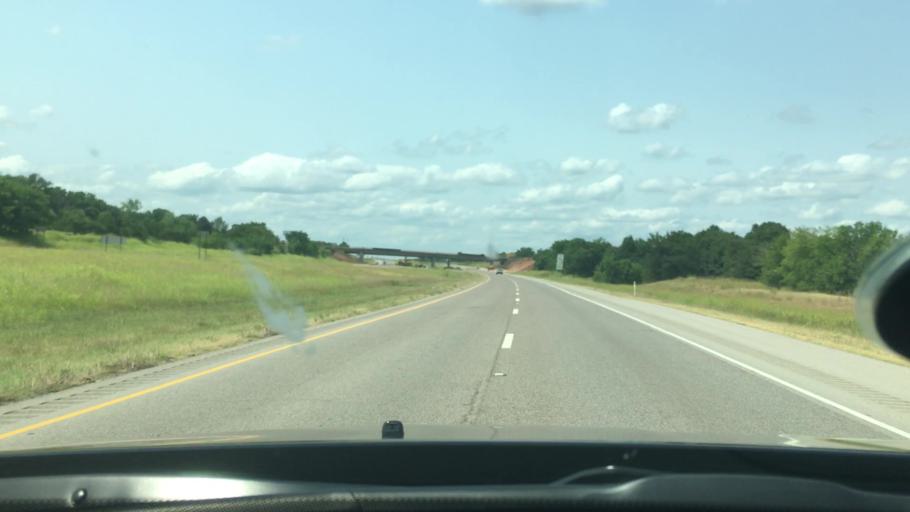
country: US
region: Oklahoma
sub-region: Murray County
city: Davis
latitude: 34.4838
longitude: -97.1587
